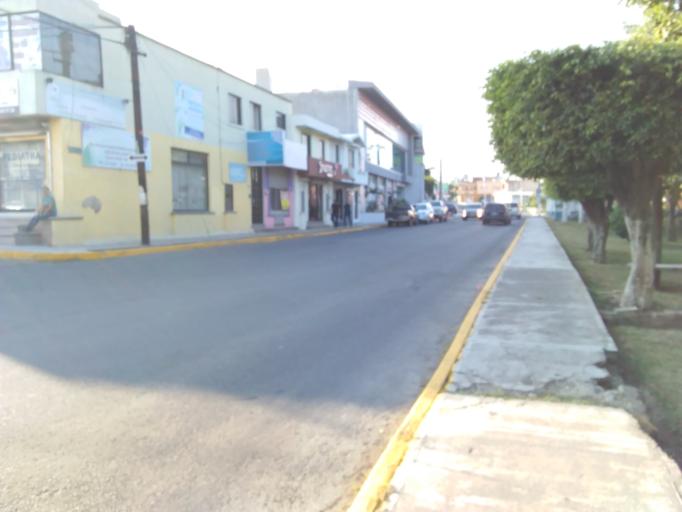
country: MX
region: Nayarit
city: Tepic
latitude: 21.5023
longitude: -104.9058
